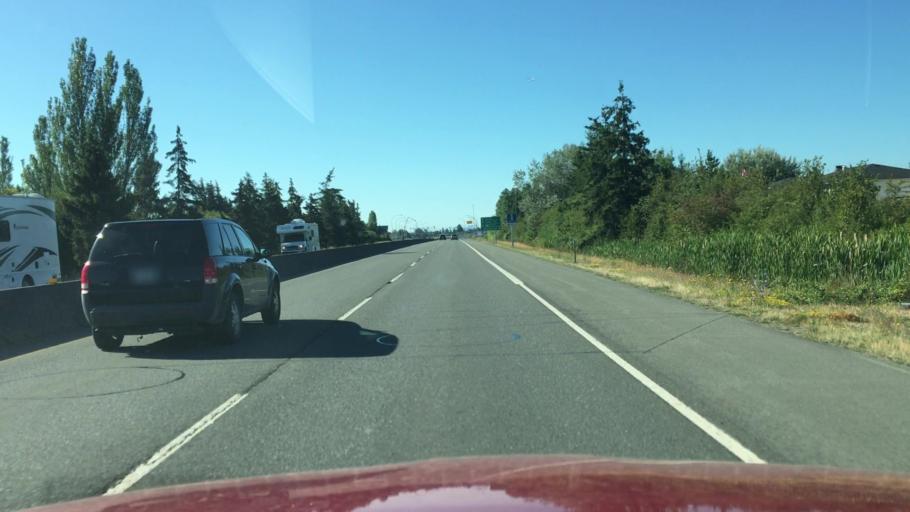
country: CA
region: British Columbia
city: North Saanich
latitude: 48.6533
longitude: -123.4103
